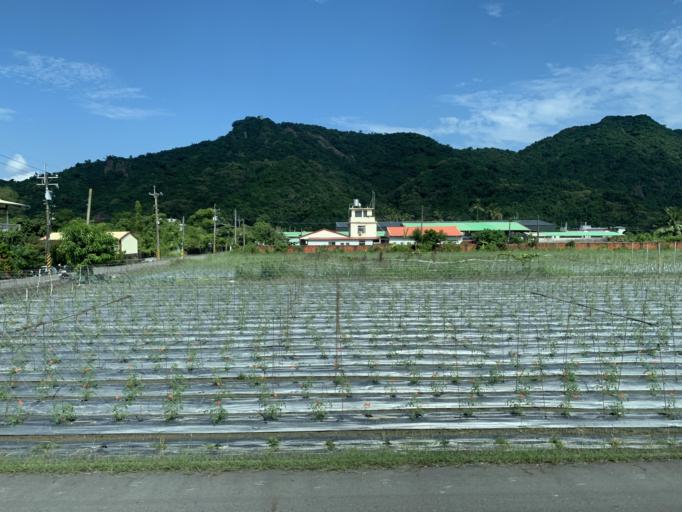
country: TW
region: Taiwan
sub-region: Pingtung
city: Pingtung
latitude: 22.8885
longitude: 120.5034
